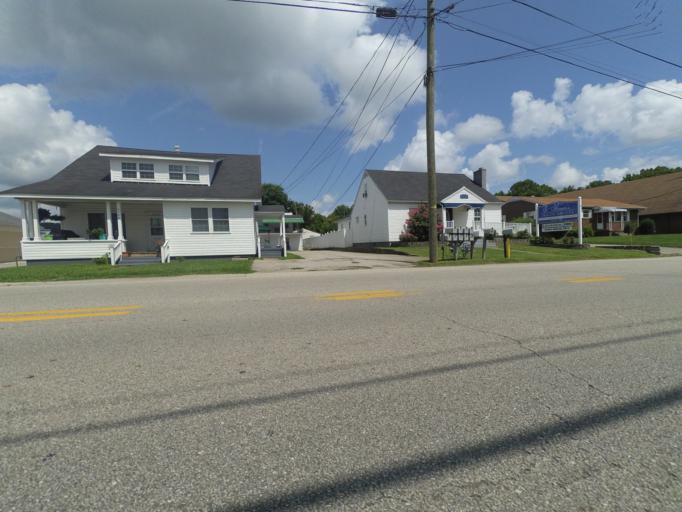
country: US
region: West Virginia
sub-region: Cabell County
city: Barboursville
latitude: 38.4131
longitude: -82.2987
